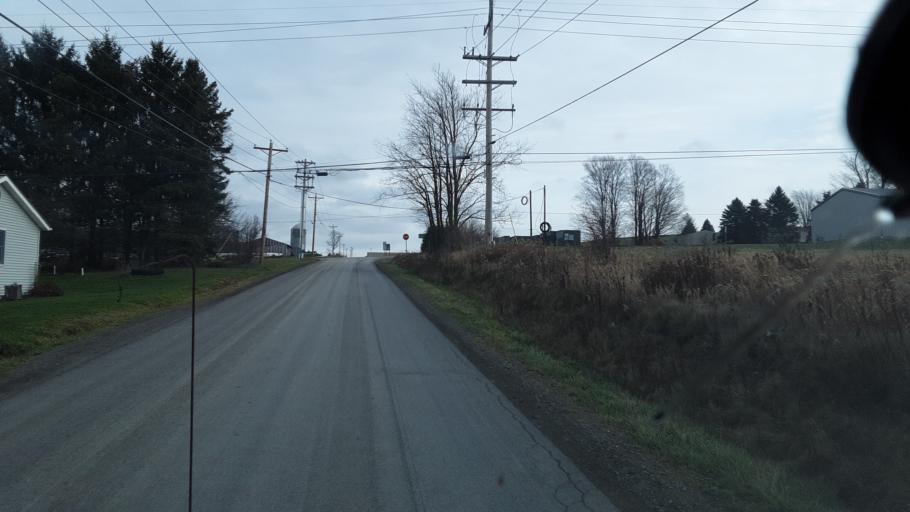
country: US
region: Pennsylvania
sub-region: Potter County
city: Galeton
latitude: 41.8866
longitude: -77.7626
